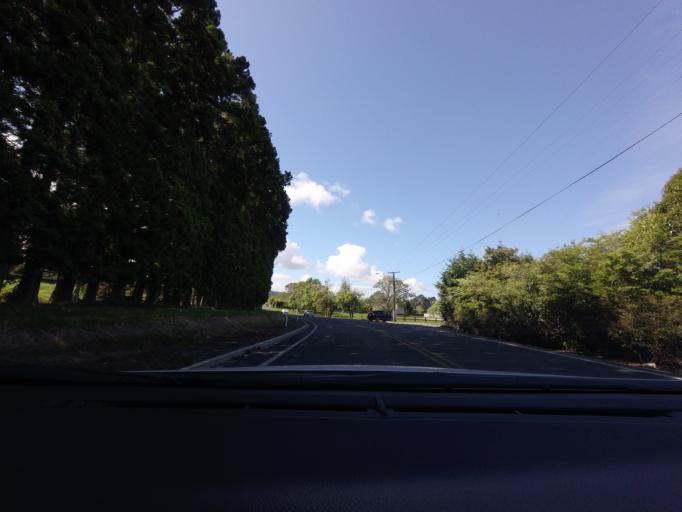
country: NZ
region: Auckland
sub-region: Auckland
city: Rosebank
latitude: -36.7765
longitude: 174.5872
